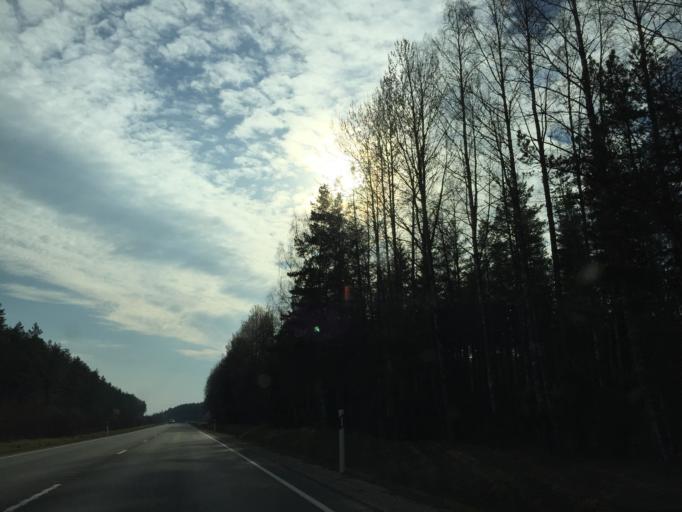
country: EE
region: Jogevamaa
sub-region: Mustvee linn
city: Mustvee
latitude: 58.9691
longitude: 27.1142
